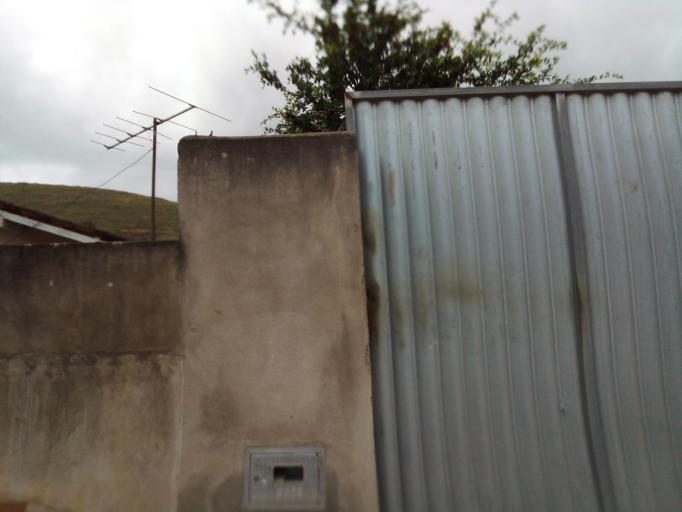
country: BR
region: Espirito Santo
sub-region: Joao Neiva
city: Joao Neiva
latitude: -19.7453
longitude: -40.3652
